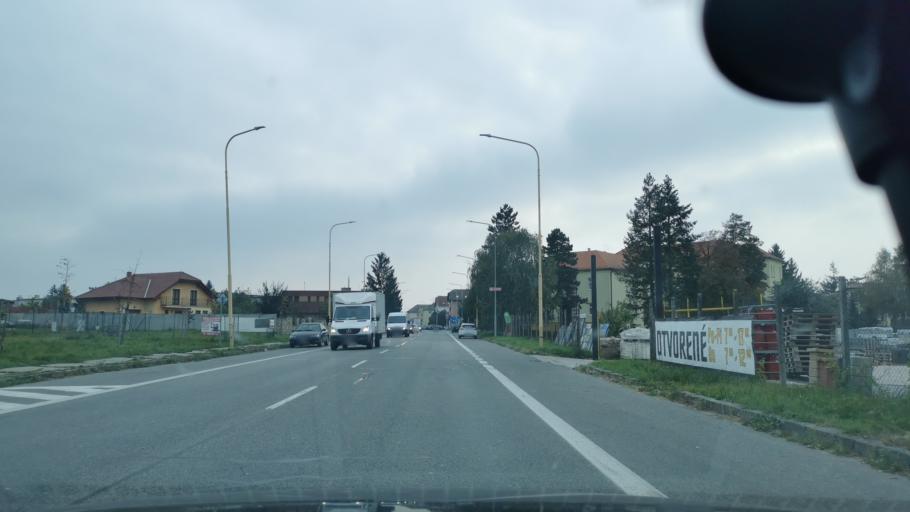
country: SK
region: Trnavsky
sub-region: Okres Skalica
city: Holic
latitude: 48.8214
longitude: 17.1644
